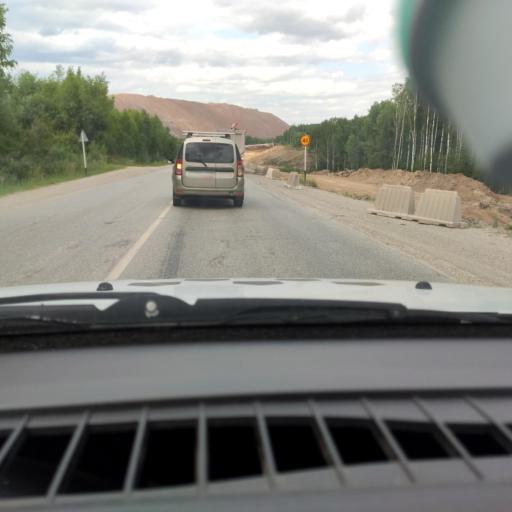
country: RU
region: Perm
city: Solikamsk
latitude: 59.5626
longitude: 56.7776
